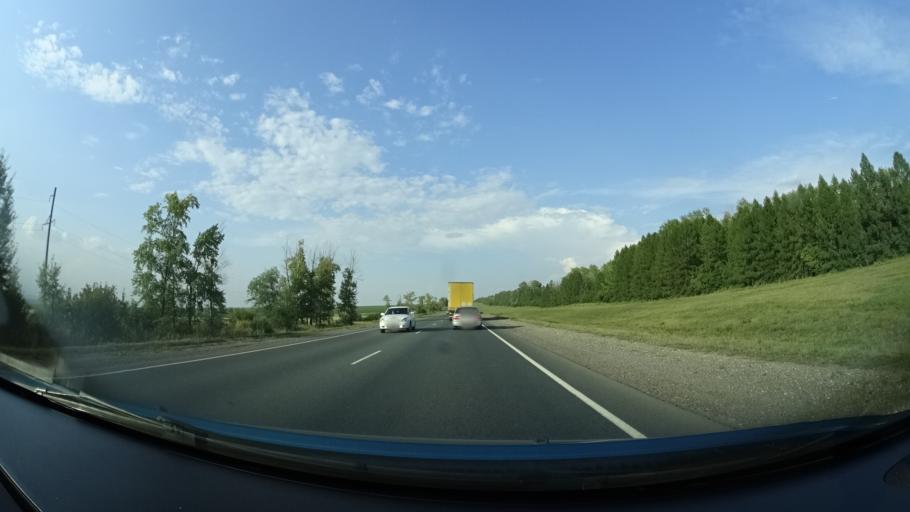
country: RU
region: Samara
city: Krasnyy Yar
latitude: 53.6547
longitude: 50.7470
